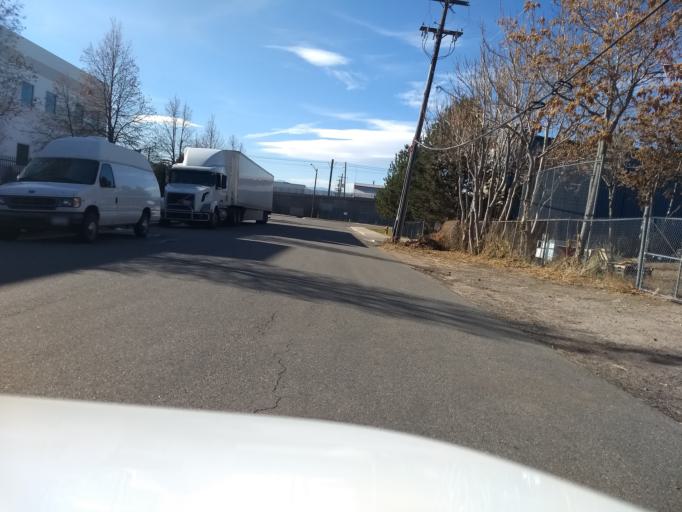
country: US
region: Colorado
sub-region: Denver County
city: Denver
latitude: 39.7166
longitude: -104.9966
